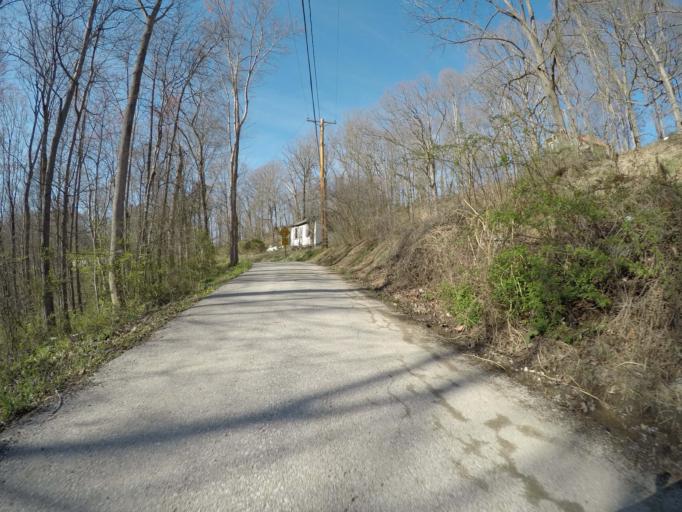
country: US
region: West Virginia
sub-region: Kanawha County
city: Charleston
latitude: 38.3803
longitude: -81.6043
